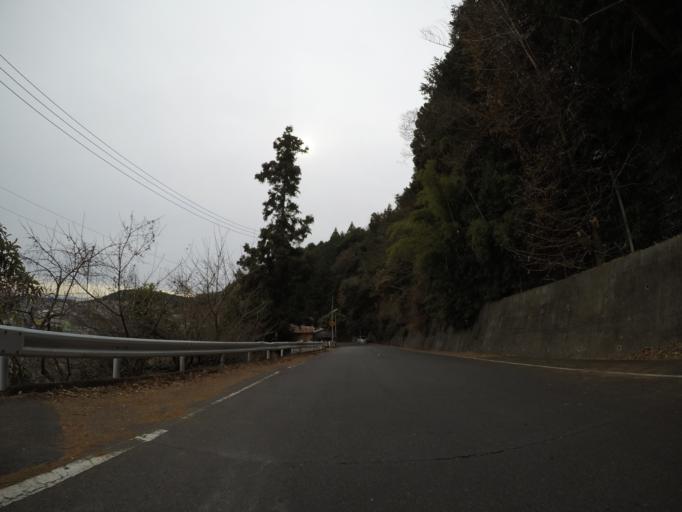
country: JP
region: Shizuoka
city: Fujinomiya
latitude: 35.2273
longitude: 138.5903
